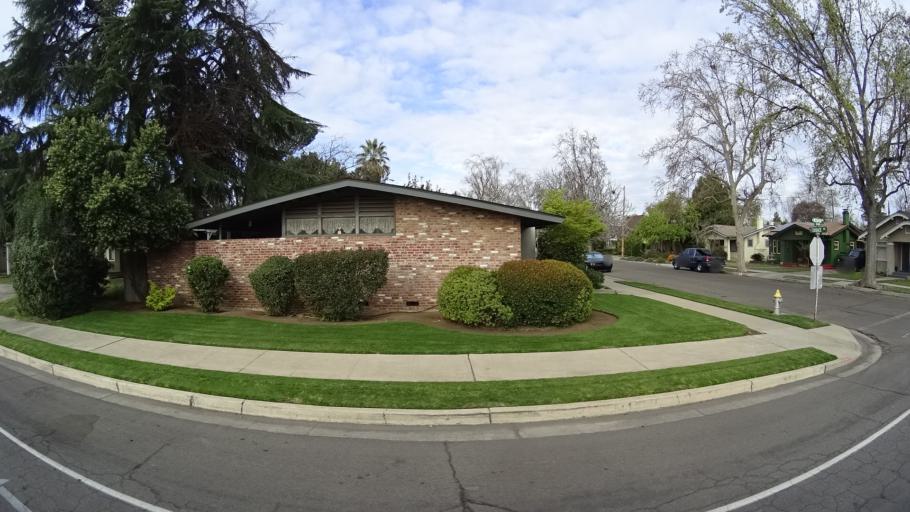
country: US
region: California
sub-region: Fresno County
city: Fresno
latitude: 36.7731
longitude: -119.8011
